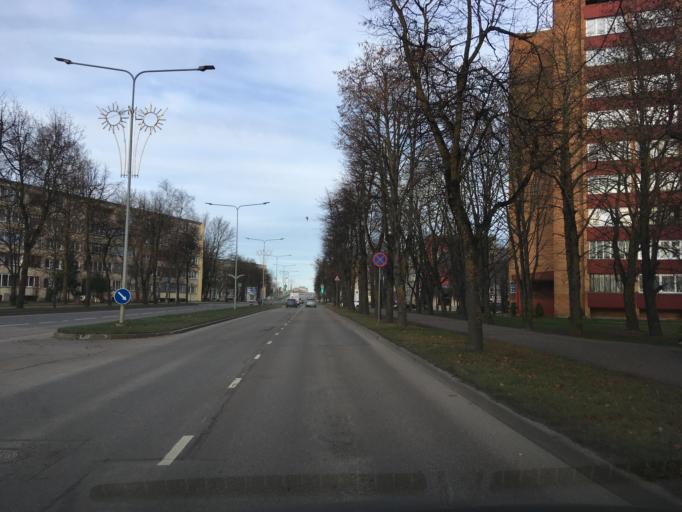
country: EE
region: Ida-Virumaa
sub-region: Narva linn
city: Narva
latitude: 59.3675
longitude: 28.1866
